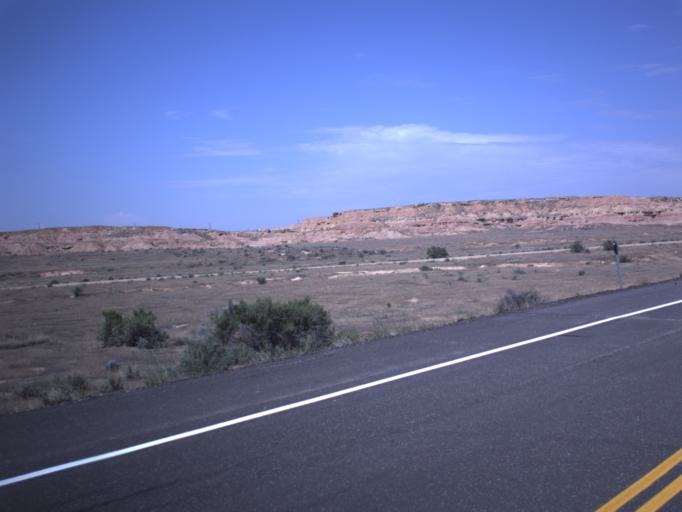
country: US
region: Utah
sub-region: Uintah County
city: Naples
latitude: 40.1210
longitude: -109.2562
